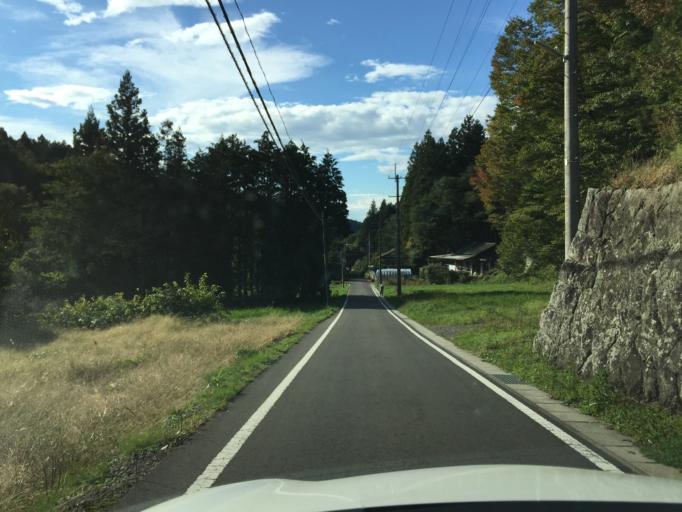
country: JP
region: Fukushima
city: Ishikawa
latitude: 37.1736
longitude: 140.4760
